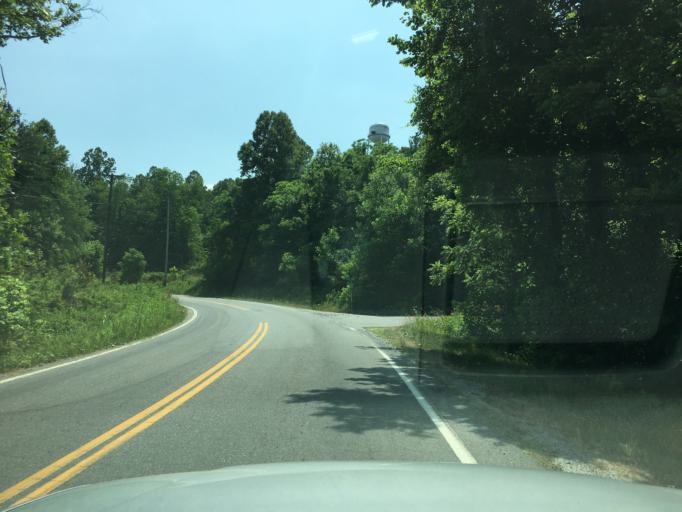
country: US
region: North Carolina
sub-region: McDowell County
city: Marion
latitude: 35.6462
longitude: -81.9536
